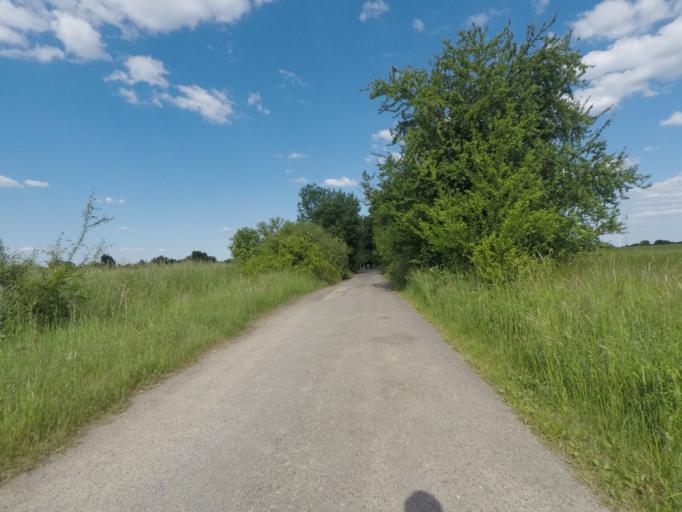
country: DE
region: Brandenburg
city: Britz
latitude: 52.8751
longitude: 13.7233
